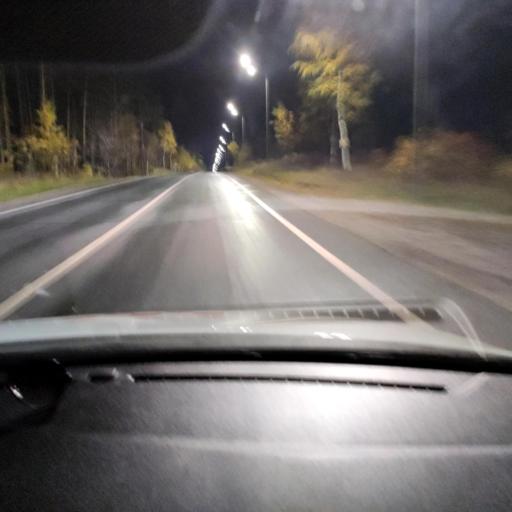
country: RU
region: Tatarstan
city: Verkhniy Uslon
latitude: 55.6395
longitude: 49.0300
